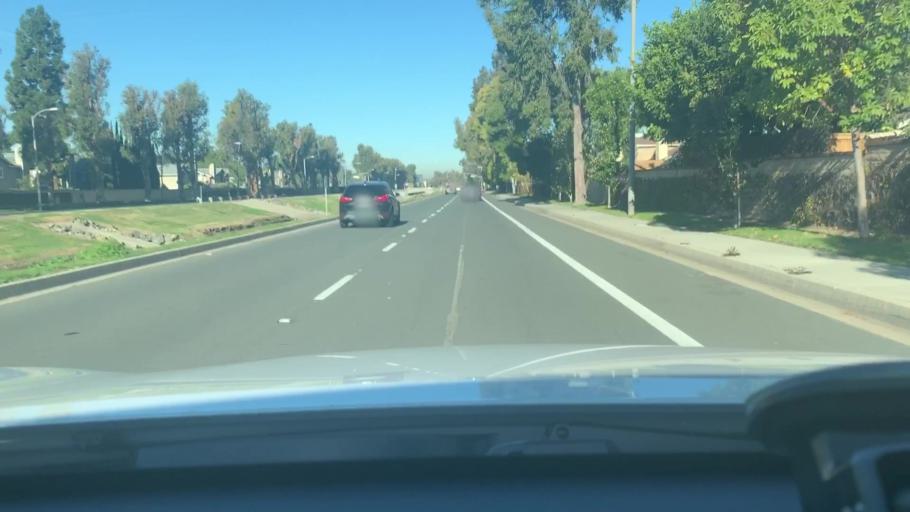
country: US
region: California
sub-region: Orange County
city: Irvine
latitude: 33.7051
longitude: -117.7739
